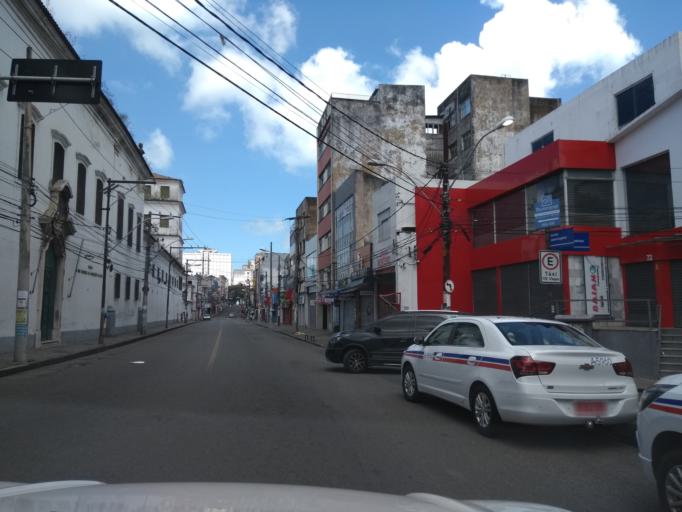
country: BR
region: Bahia
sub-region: Salvador
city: Salvador
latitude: -12.9809
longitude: -38.5122
